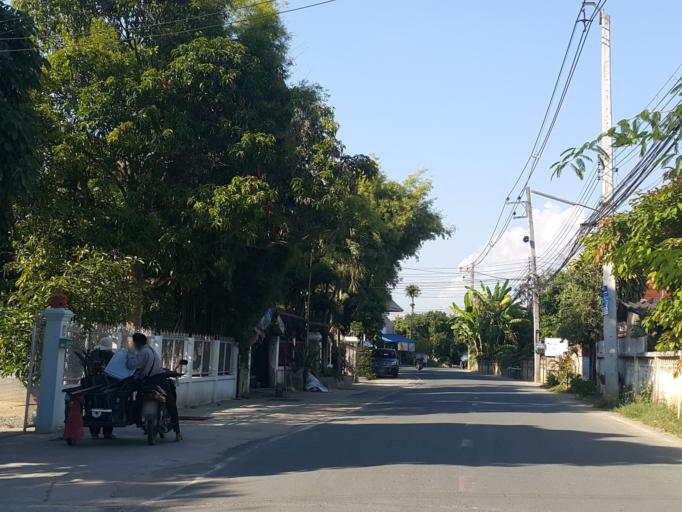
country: TH
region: Chiang Mai
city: San Sai
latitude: 18.7922
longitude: 99.0459
